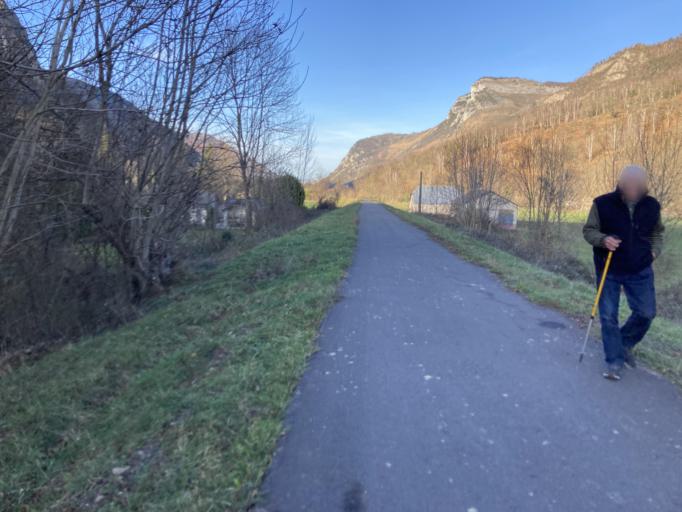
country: FR
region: Aquitaine
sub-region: Departement des Pyrenees-Atlantiques
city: Laruns
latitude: 43.0031
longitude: -0.4194
